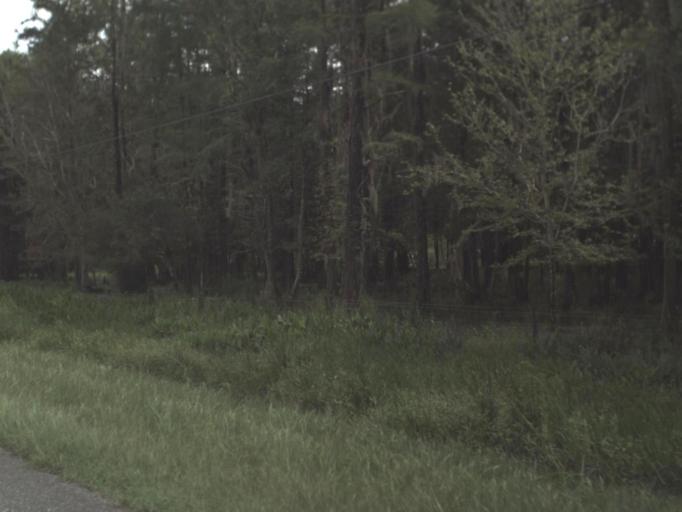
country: US
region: Florida
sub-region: Columbia County
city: Watertown
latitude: 30.0454
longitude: -82.5983
